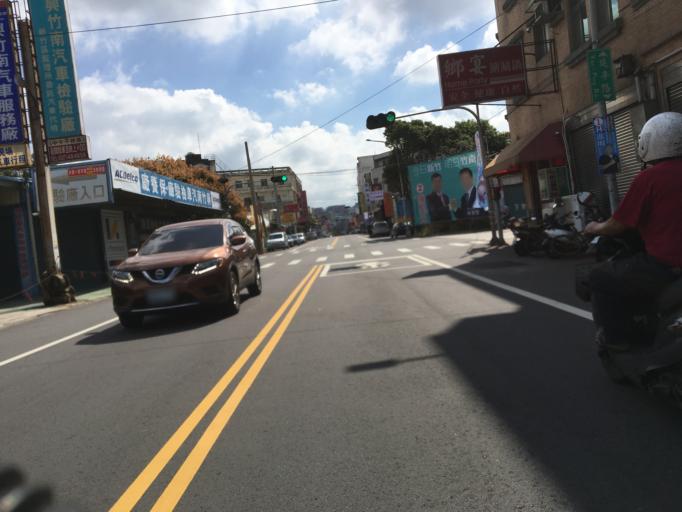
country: TW
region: Taiwan
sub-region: Miaoli
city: Miaoli
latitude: 24.6907
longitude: 120.8742
